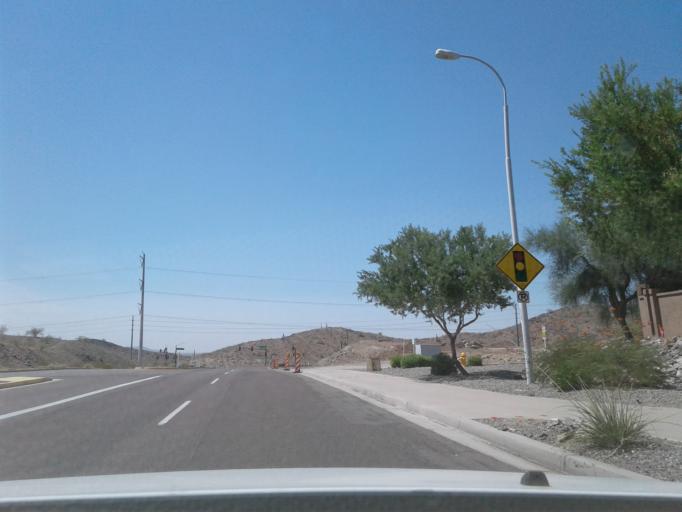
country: US
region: Arizona
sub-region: Maricopa County
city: Laveen
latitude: 33.2932
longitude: -112.0637
